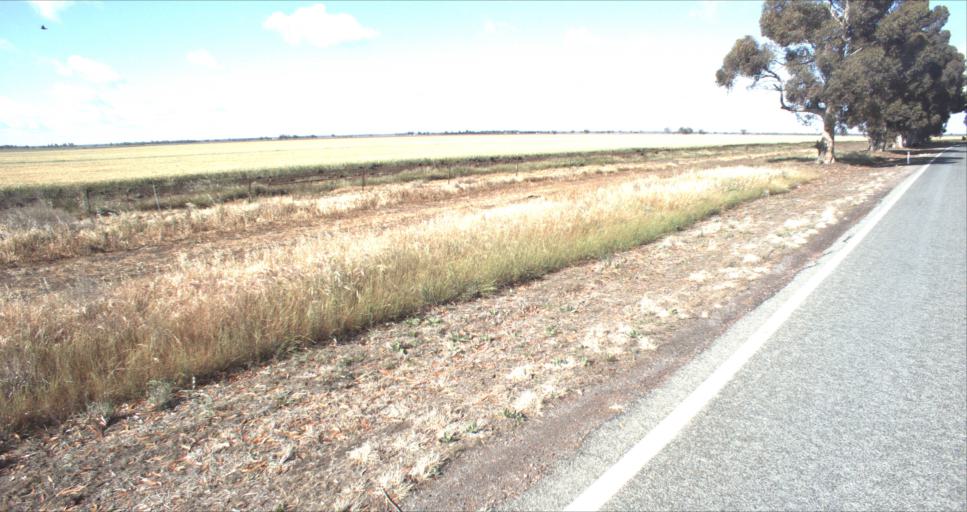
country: AU
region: New South Wales
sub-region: Leeton
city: Leeton
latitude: -34.5486
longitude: 146.3210
